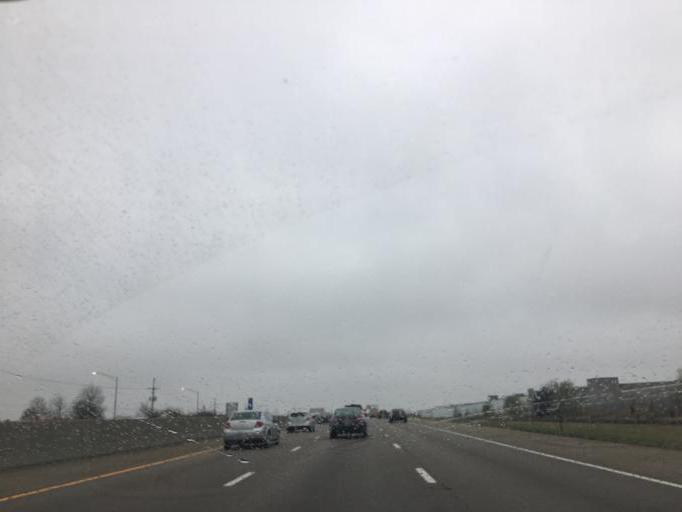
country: US
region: Kansas
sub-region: Johnson County
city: Olathe
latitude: 38.9040
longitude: -94.7810
